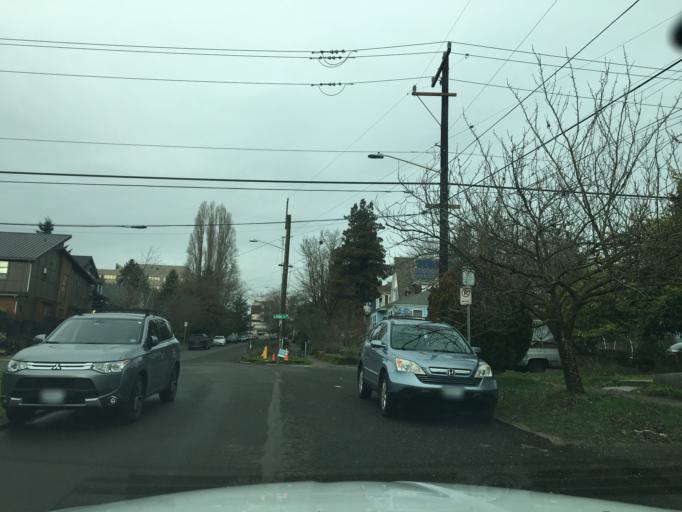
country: US
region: Washington
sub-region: King County
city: Seattle
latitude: 47.6041
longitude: -122.3102
